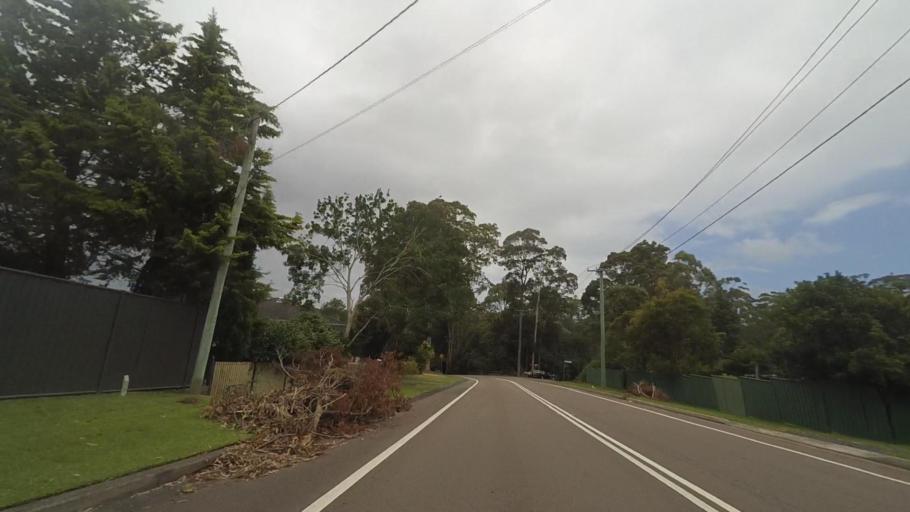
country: AU
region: New South Wales
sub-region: Wyong Shire
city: Berkeley Vale
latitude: -33.3409
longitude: 151.4203
